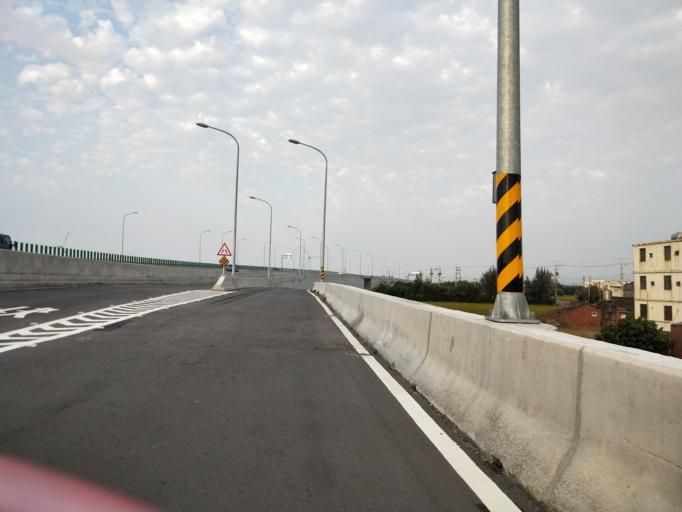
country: TW
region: Taiwan
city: Fengyuan
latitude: 24.3874
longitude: 120.5950
